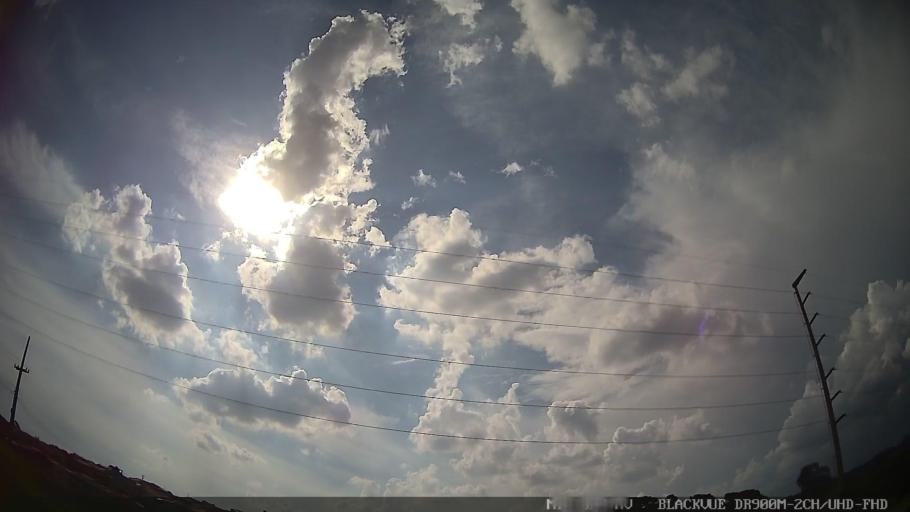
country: BR
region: Sao Paulo
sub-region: Braganca Paulista
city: Braganca Paulista
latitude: -22.9101
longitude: -46.5463
